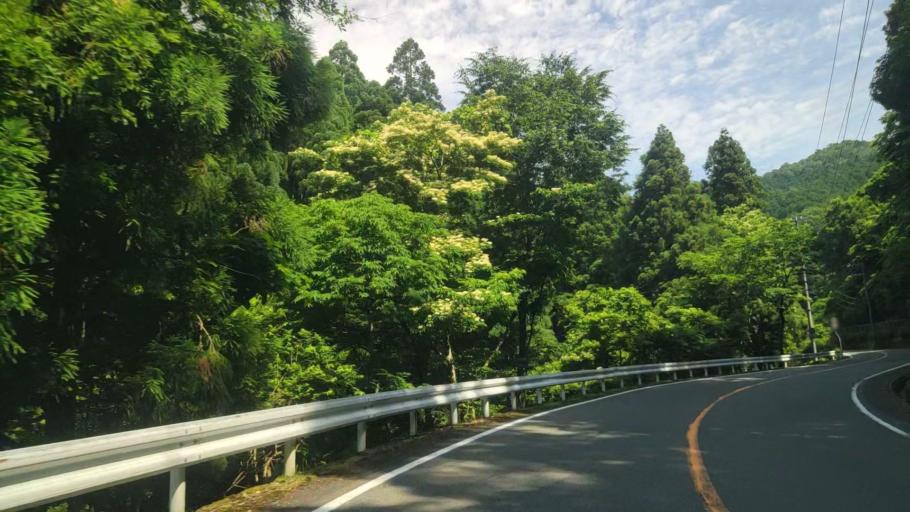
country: JP
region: Hyogo
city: Toyooka
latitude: 35.6336
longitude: 134.7804
